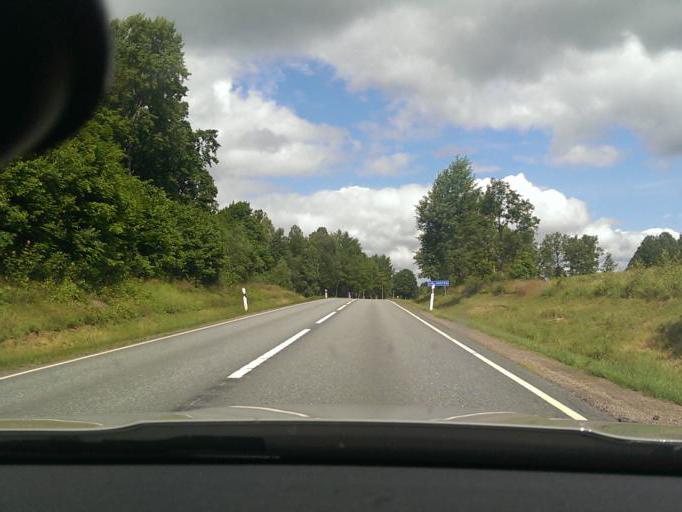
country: SE
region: Joenkoeping
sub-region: Varnamo Kommun
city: Varnamo
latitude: 57.2245
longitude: 14.0092
